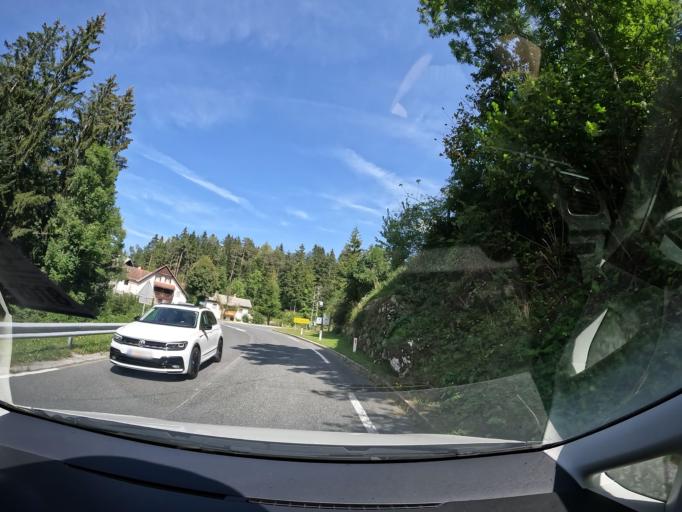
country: AT
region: Carinthia
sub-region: Politischer Bezirk Klagenfurt Land
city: Schiefling am See
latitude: 46.6314
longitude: 14.1192
